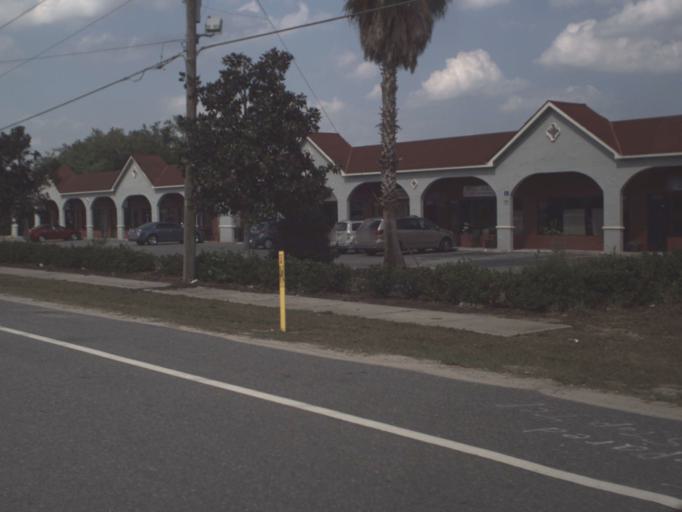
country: US
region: Florida
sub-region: Lake County
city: Tavares
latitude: 28.7774
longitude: -81.7487
